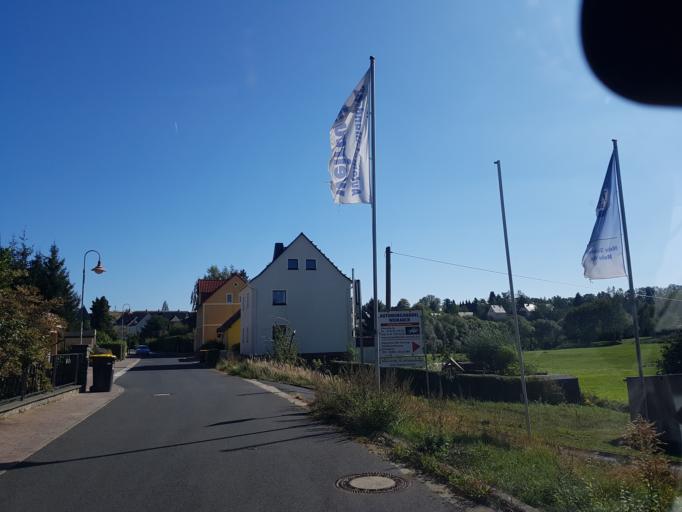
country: DE
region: Saxony
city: Waldheim
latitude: 51.0764
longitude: 13.0040
